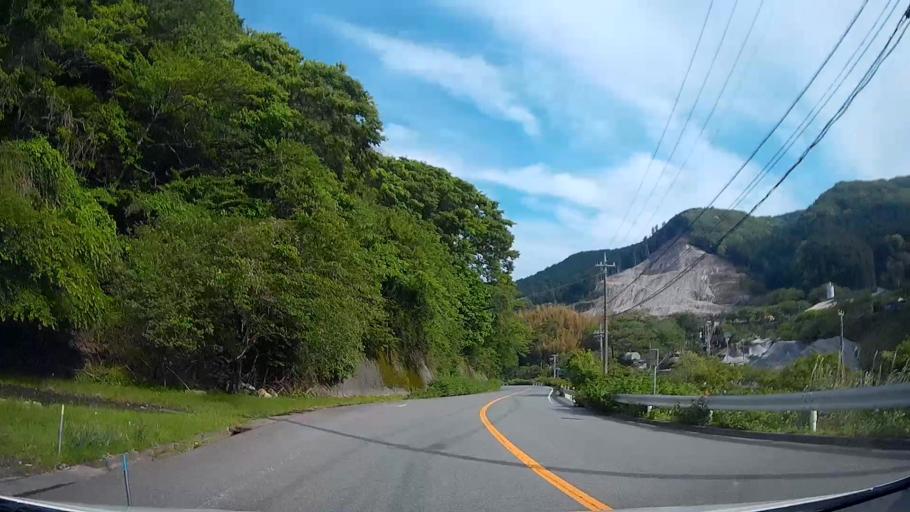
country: JP
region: Shizuoka
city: Heda
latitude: 34.9163
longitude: 138.8764
